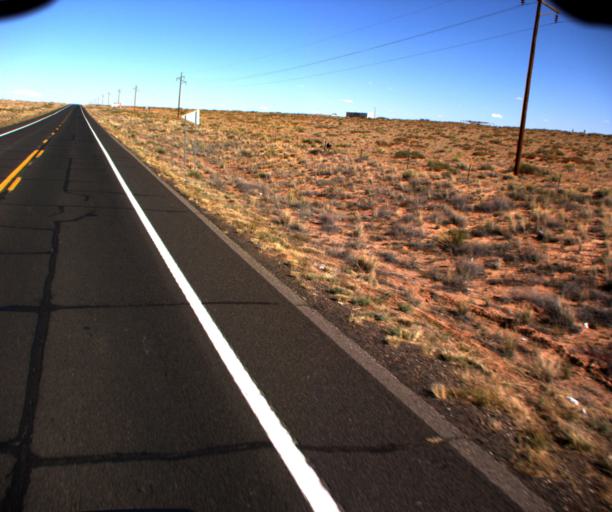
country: US
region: Arizona
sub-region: Coconino County
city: Tuba City
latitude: 36.1412
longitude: -111.1598
